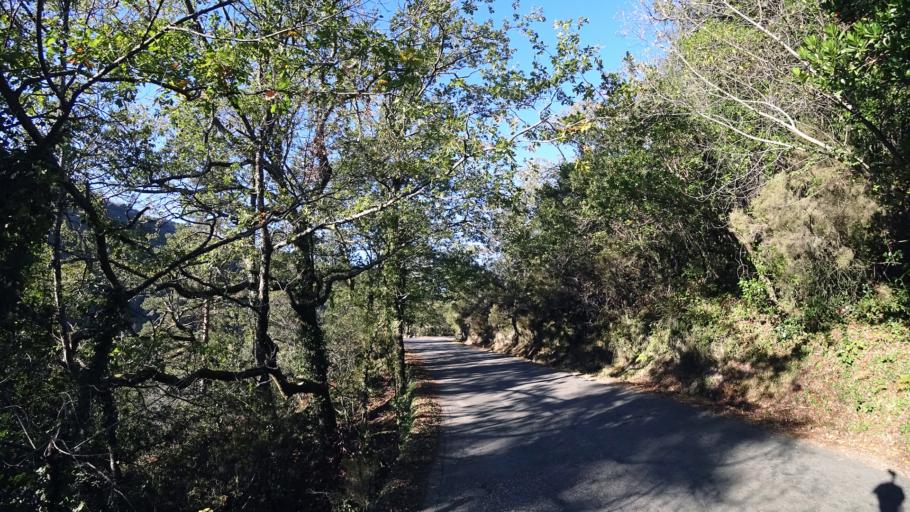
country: ES
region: Galicia
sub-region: Provincia de Ourense
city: Lobios
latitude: 41.8010
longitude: -8.1316
